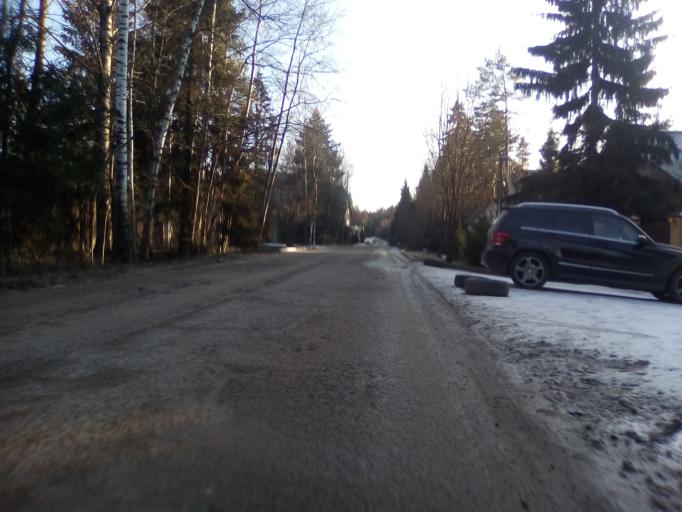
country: RU
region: Moskovskaya
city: Kokoshkino
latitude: 55.6354
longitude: 37.1476
